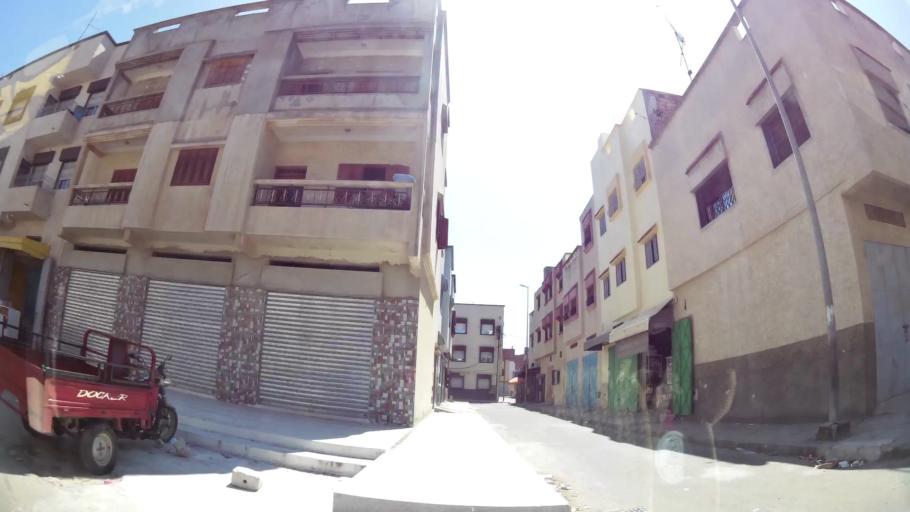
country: MA
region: Gharb-Chrarda-Beni Hssen
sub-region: Kenitra Province
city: Kenitra
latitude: 34.2397
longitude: -6.5518
